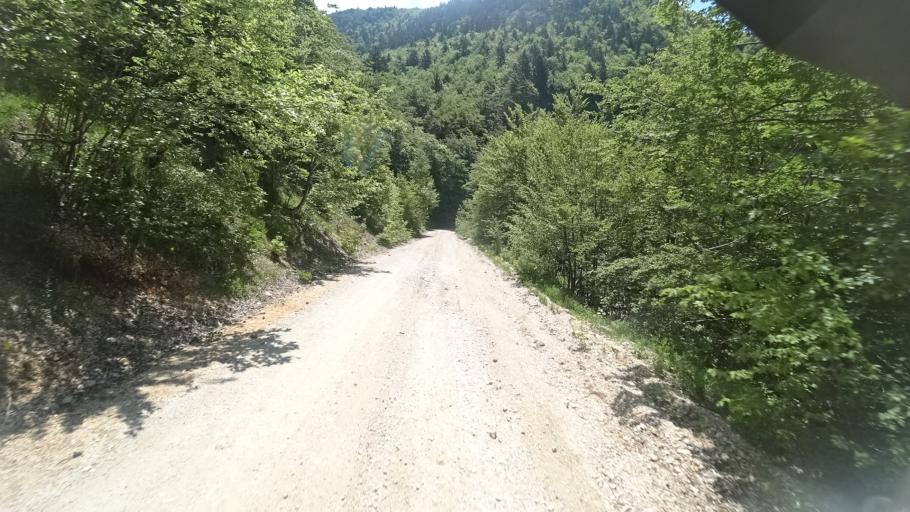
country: BA
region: Federation of Bosnia and Herzegovina
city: Orasac
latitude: 44.5729
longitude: 15.8580
